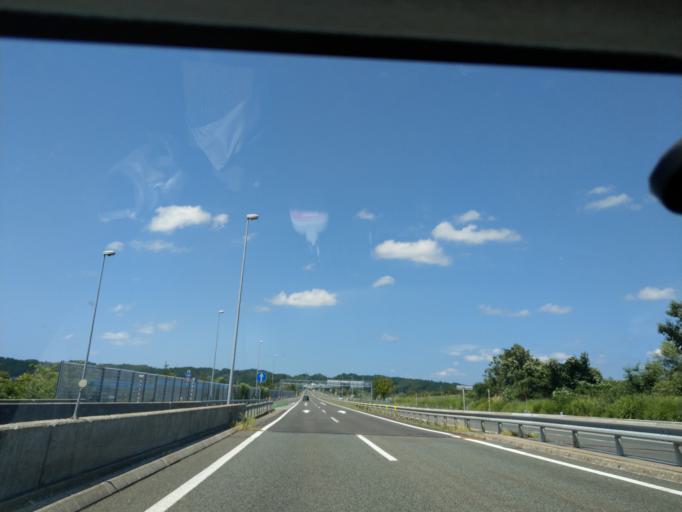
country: JP
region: Akita
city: Akita
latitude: 39.6423
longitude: 140.2102
